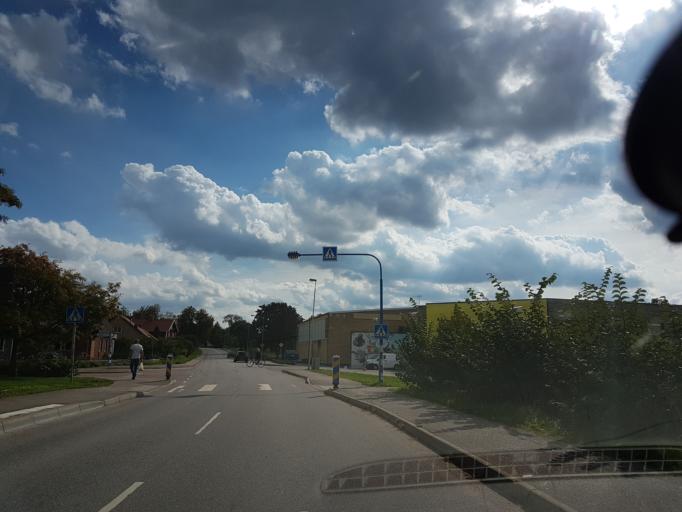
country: SE
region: OEstergoetland
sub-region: Linkopings Kommun
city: Vikingstad
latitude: 58.3817
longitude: 15.4364
